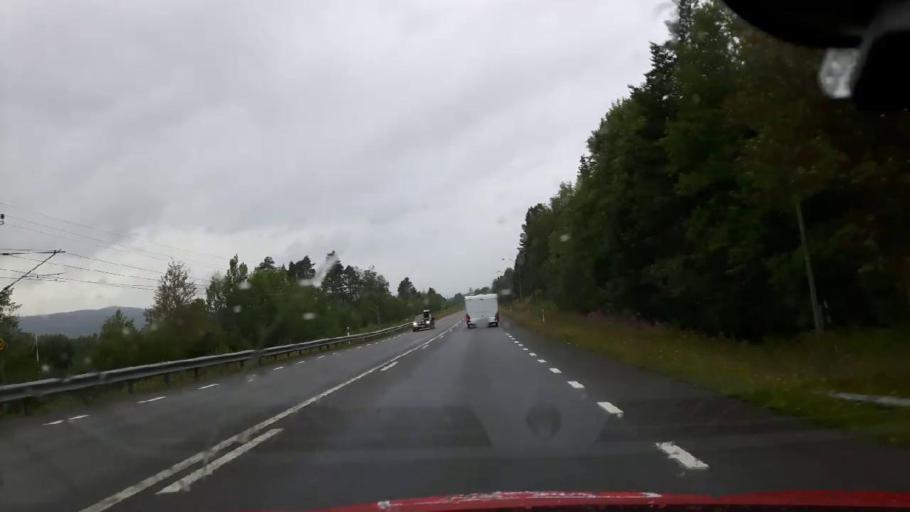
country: SE
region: Jaemtland
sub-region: Are Kommun
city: Jarpen
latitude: 63.3090
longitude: 13.6184
